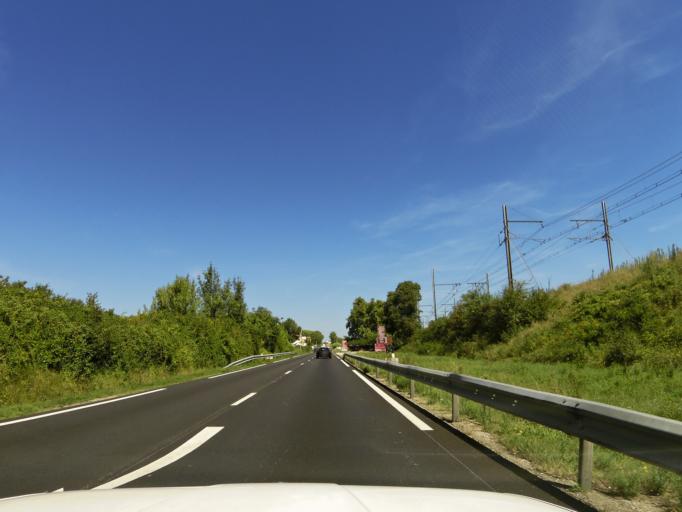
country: FR
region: Languedoc-Roussillon
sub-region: Departement du Gard
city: Saint-Nazaire
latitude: 44.1811
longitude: 4.6200
